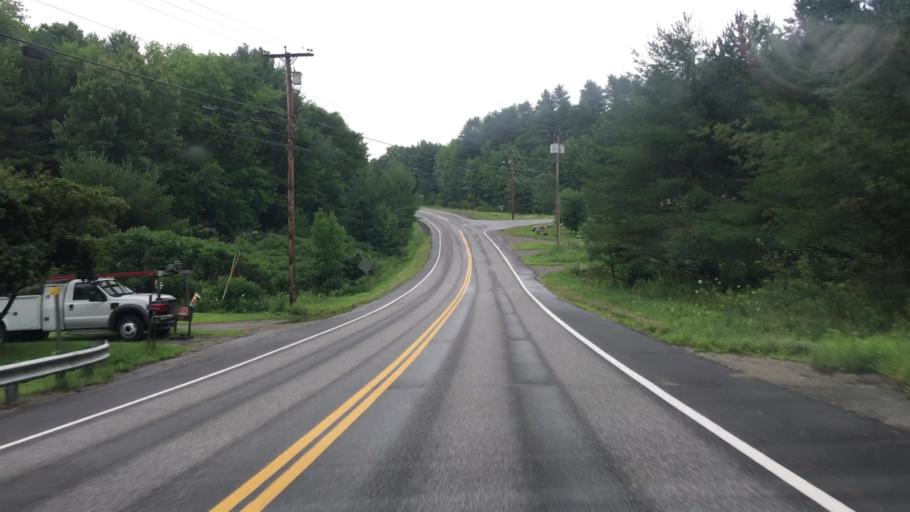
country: US
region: Maine
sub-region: Kennebec County
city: Augusta
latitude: 44.3394
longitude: -69.8109
